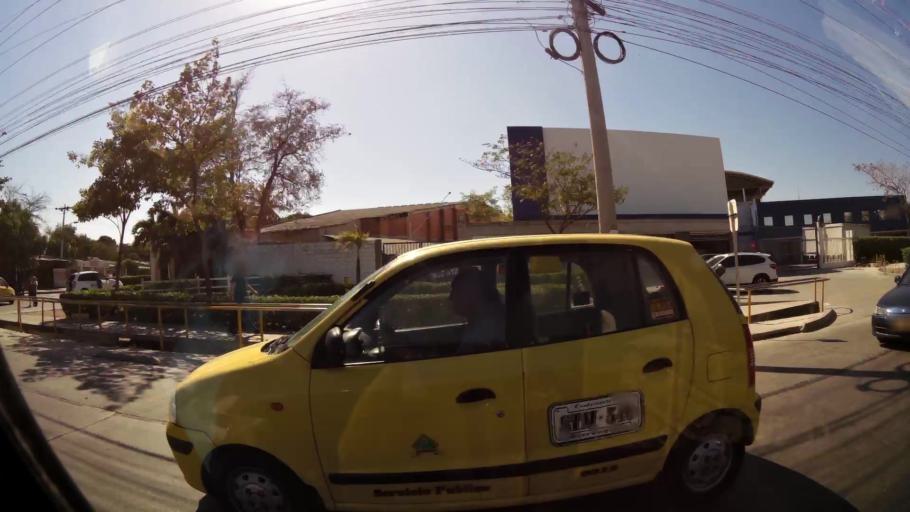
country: CO
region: Atlantico
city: Soledad
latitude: 10.9383
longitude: -74.7824
